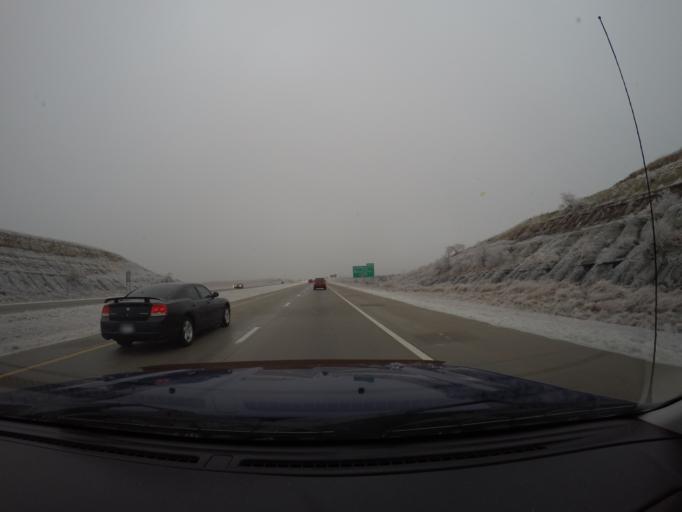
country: US
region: Kansas
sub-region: Riley County
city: Manhattan
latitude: 39.0628
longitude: -96.5274
